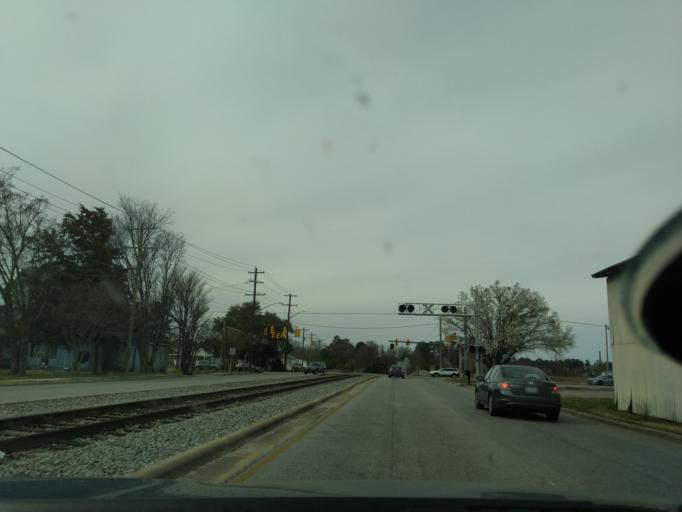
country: US
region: North Carolina
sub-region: Edgecombe County
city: Tarboro
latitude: 35.9058
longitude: -77.5429
